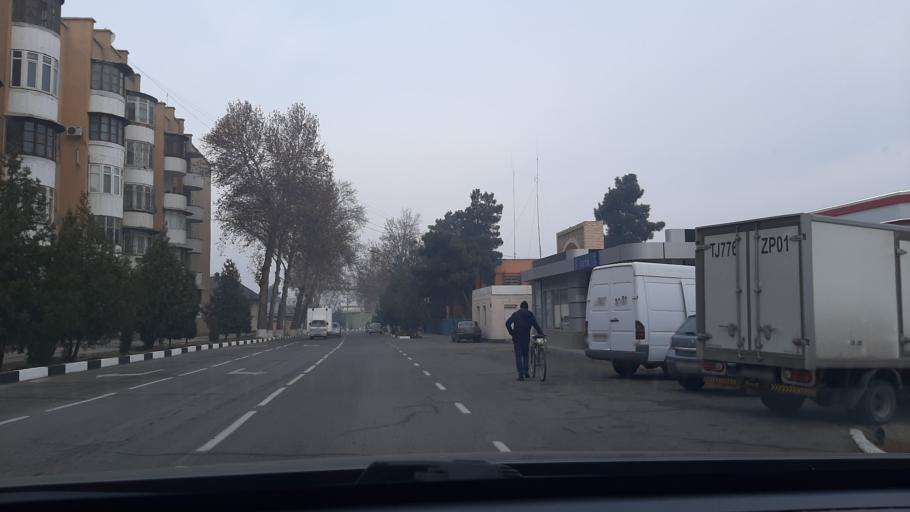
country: TJ
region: Viloyati Sughd
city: Chkalov
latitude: 40.2379
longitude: 69.7023
